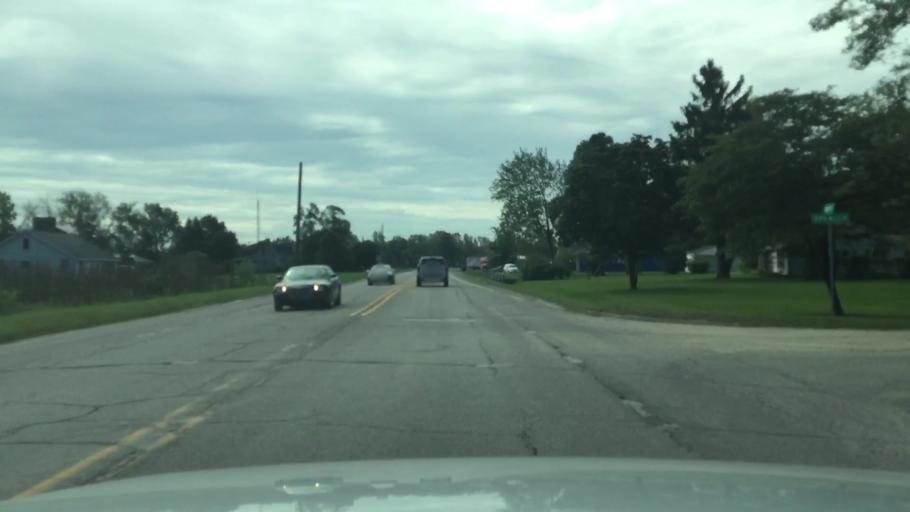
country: US
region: Michigan
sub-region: Wayne County
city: Belleville
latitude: 42.1933
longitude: -83.4841
